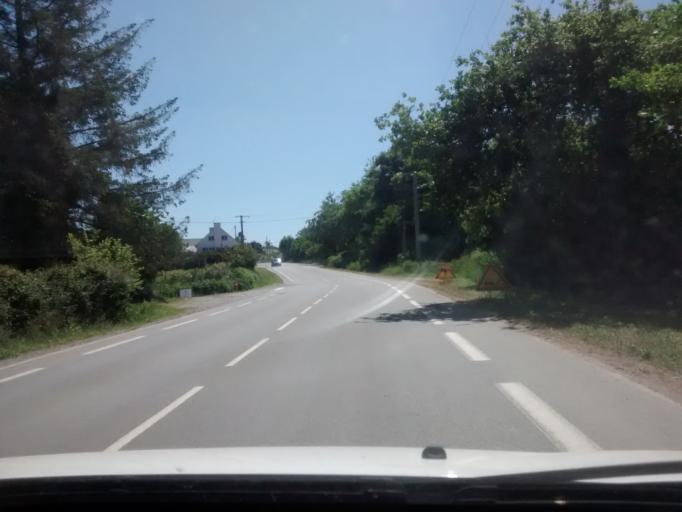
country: FR
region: Brittany
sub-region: Departement d'Ille-et-Vilaine
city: Saint-Lunaire
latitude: 48.6249
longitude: -2.1064
